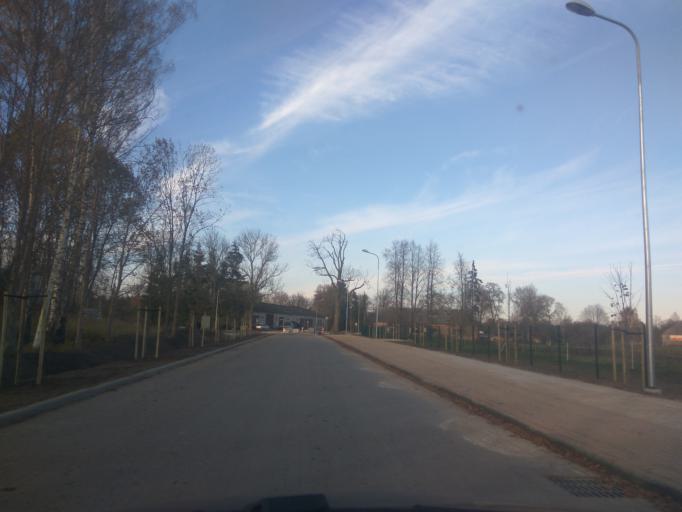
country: LV
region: Kuldigas Rajons
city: Kuldiga
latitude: 56.9850
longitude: 21.9493
